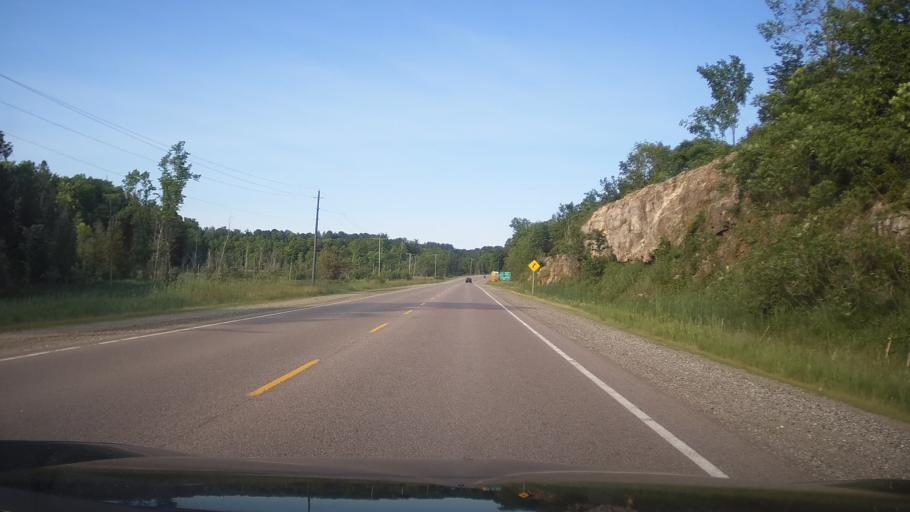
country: CA
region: Ontario
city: Skatepark
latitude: 44.7437
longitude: -76.9231
